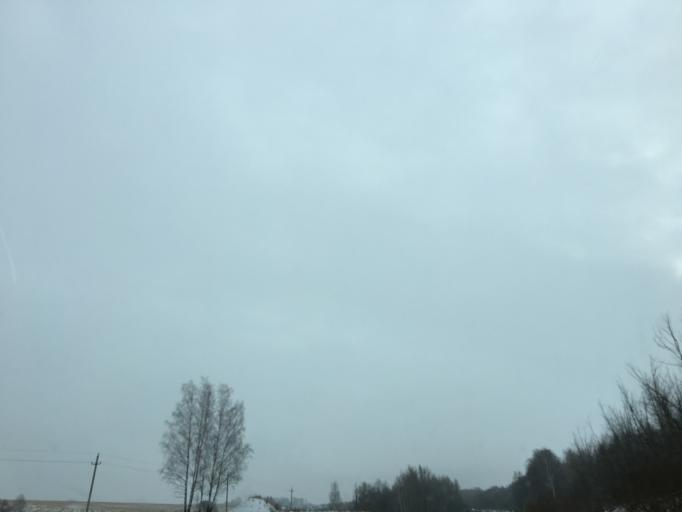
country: RU
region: Tula
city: Bolokhovo
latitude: 54.0362
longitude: 37.8757
